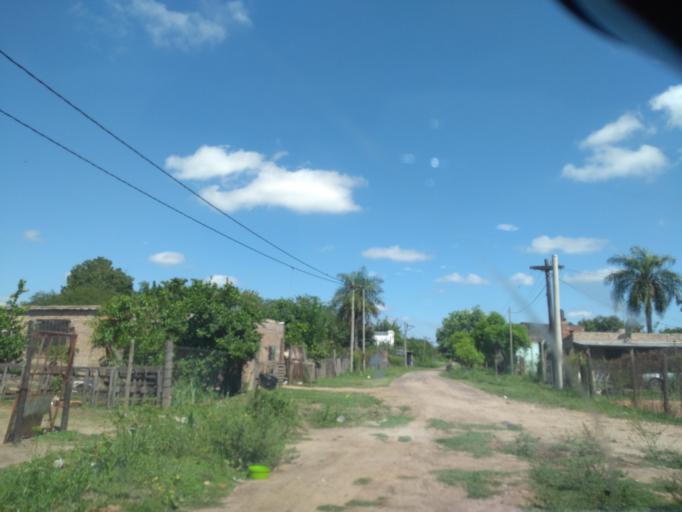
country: AR
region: Chaco
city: Fontana
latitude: -27.4064
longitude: -59.0384
